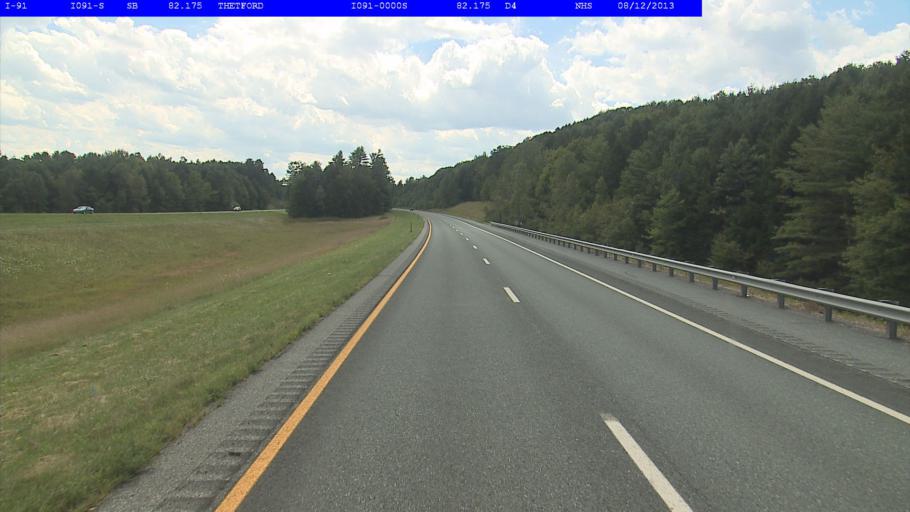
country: US
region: New Hampshire
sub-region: Grafton County
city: Lyme
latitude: 43.7852
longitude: -72.2182
